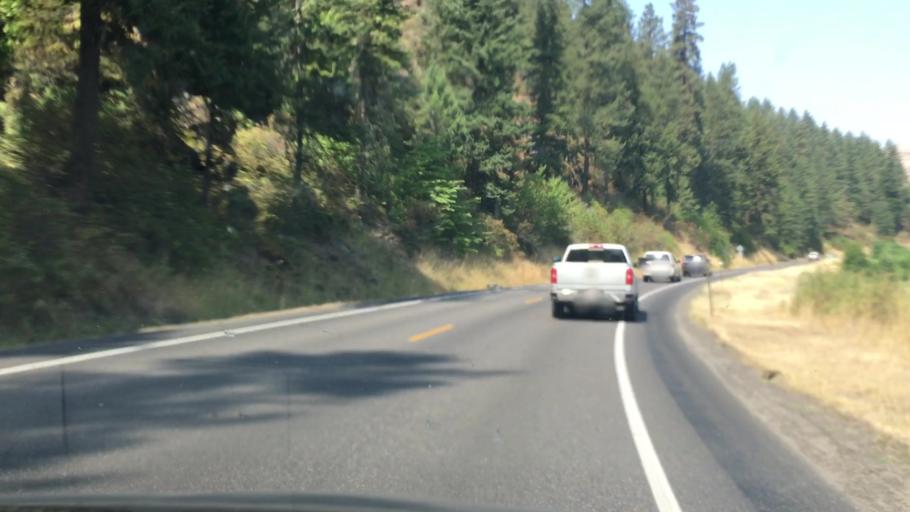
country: US
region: Idaho
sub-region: Clearwater County
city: Orofino
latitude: 46.4899
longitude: -116.4559
